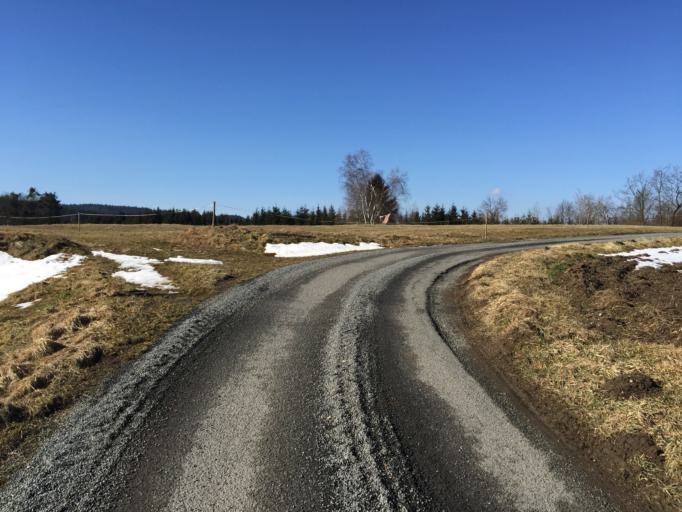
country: AT
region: Lower Austria
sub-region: Politischer Bezirk Gmund
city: Weitra
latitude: 48.6683
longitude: 14.9314
